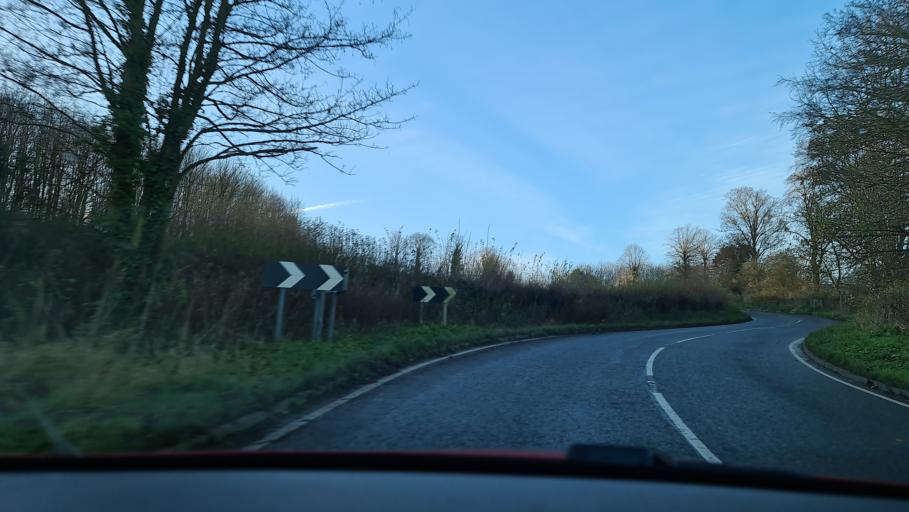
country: GB
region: England
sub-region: Buckinghamshire
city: Waddesdon
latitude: 51.8351
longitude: -0.9041
